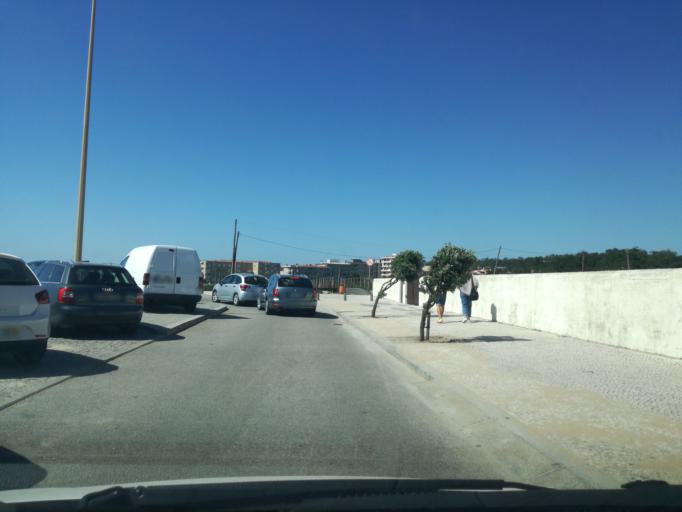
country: PT
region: Porto
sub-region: Matosinhos
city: Lavra
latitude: 41.2684
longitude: -8.7262
